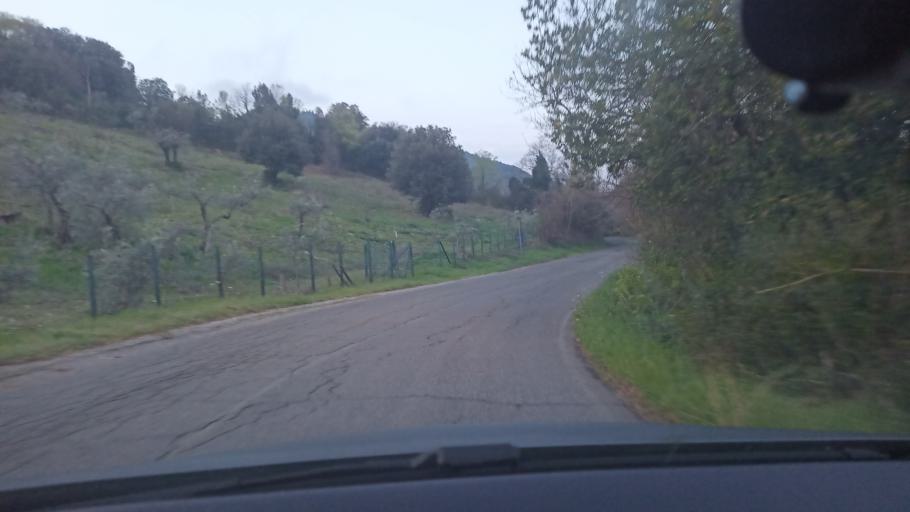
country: IT
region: Latium
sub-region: Provincia di Rieti
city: Cottanello
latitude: 42.3990
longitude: 12.6789
